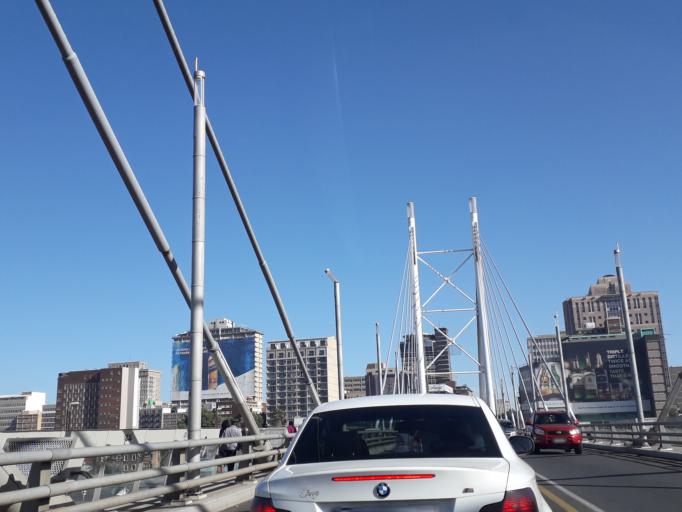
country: ZA
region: Gauteng
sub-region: City of Johannesburg Metropolitan Municipality
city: Johannesburg
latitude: -26.1974
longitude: 28.0343
